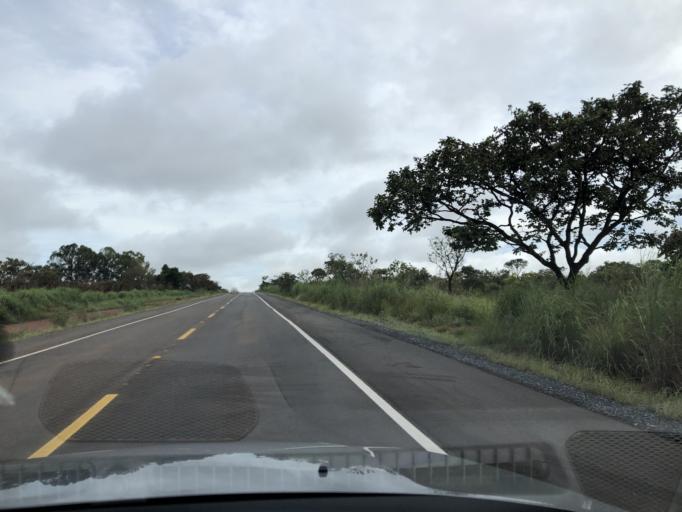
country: BR
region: Federal District
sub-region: Brasilia
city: Brasilia
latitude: -15.6387
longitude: -48.0785
